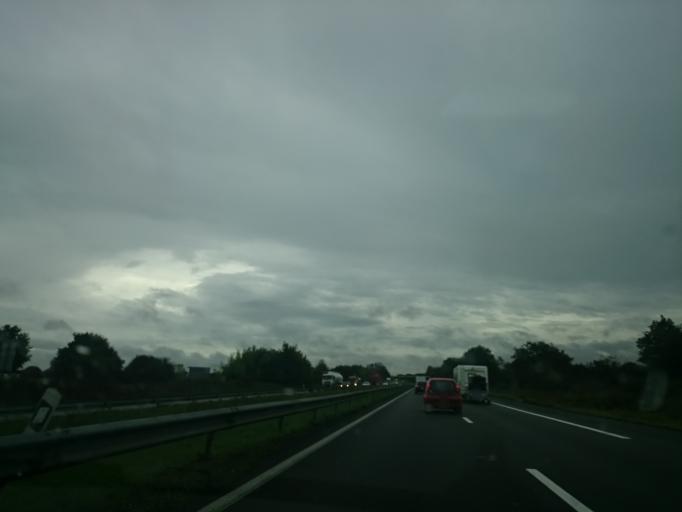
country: FR
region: Pays de la Loire
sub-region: Departement de la Loire-Atlantique
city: Sautron
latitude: 47.2735
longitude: -1.7184
